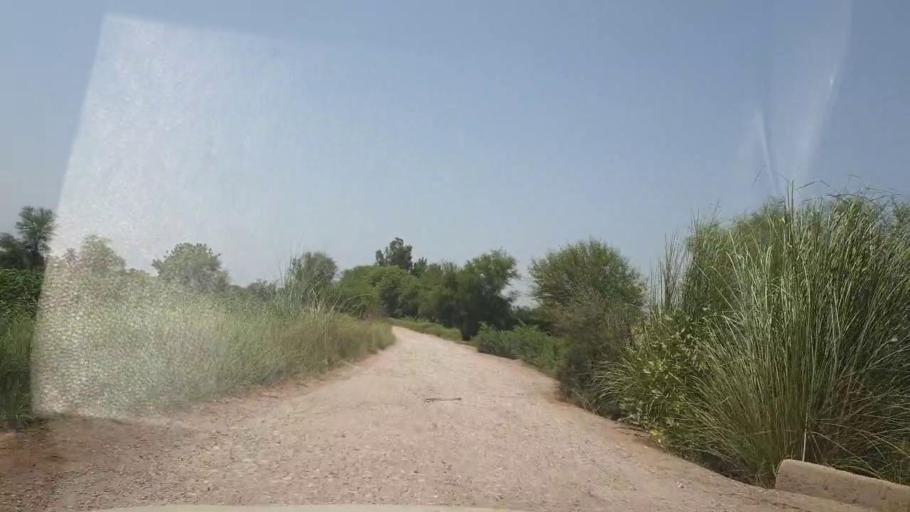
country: PK
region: Sindh
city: Bozdar
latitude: 27.1282
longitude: 68.6272
